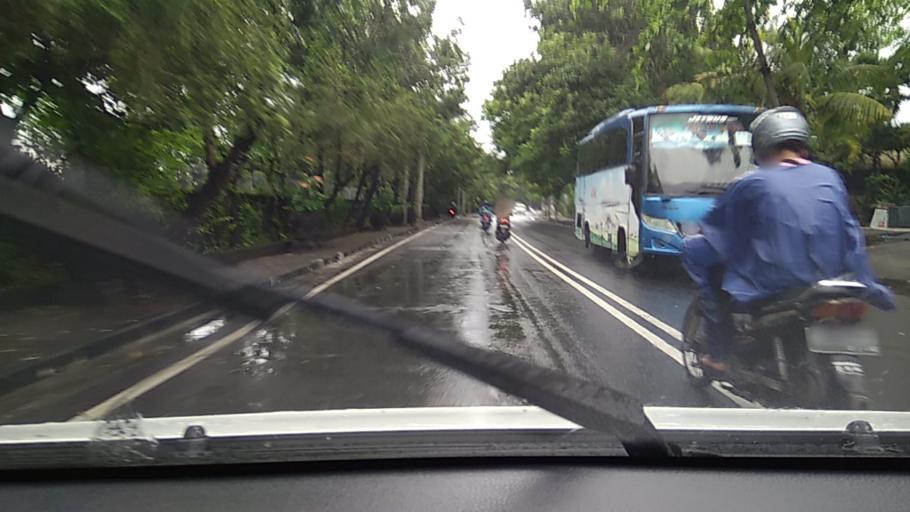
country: ID
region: Bali
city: Bualu
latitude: -8.7898
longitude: 115.2228
